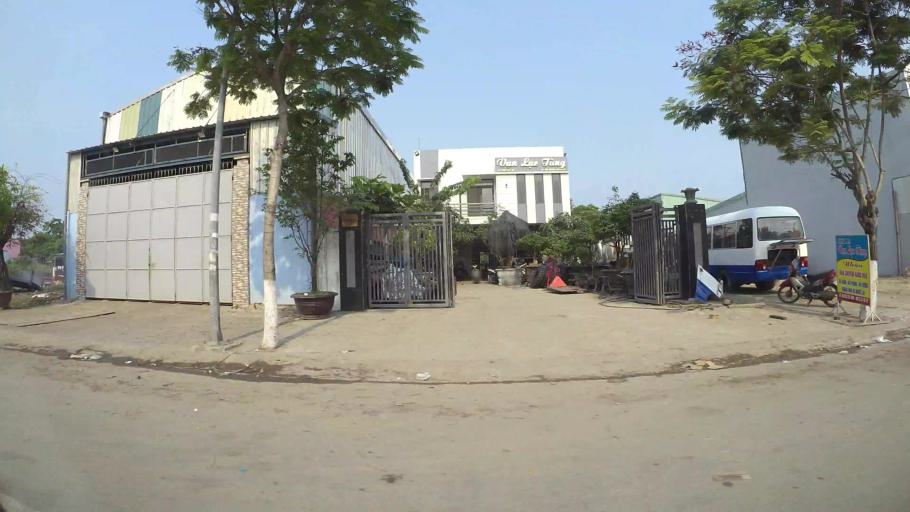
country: VN
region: Da Nang
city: Thanh Khe
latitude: 16.0505
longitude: 108.1743
